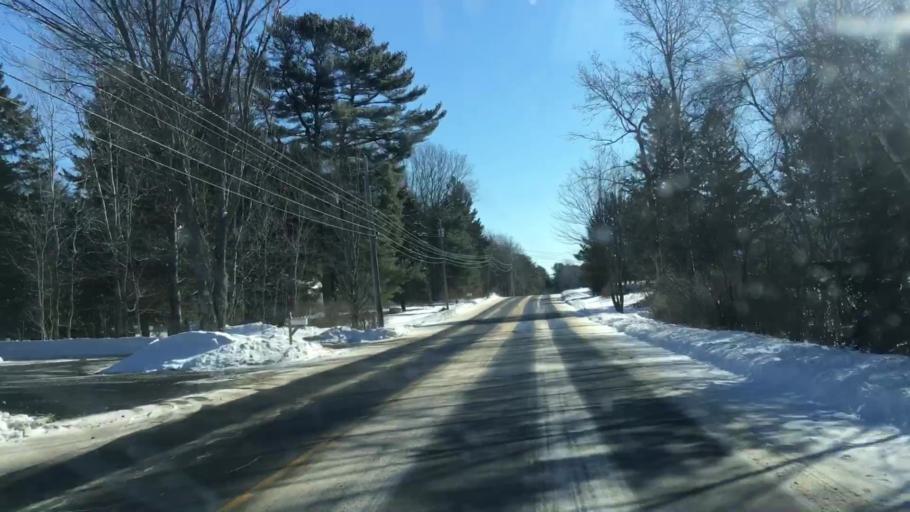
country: US
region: Maine
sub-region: Sagadahoc County
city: Topsham
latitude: 43.9066
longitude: -70.0054
